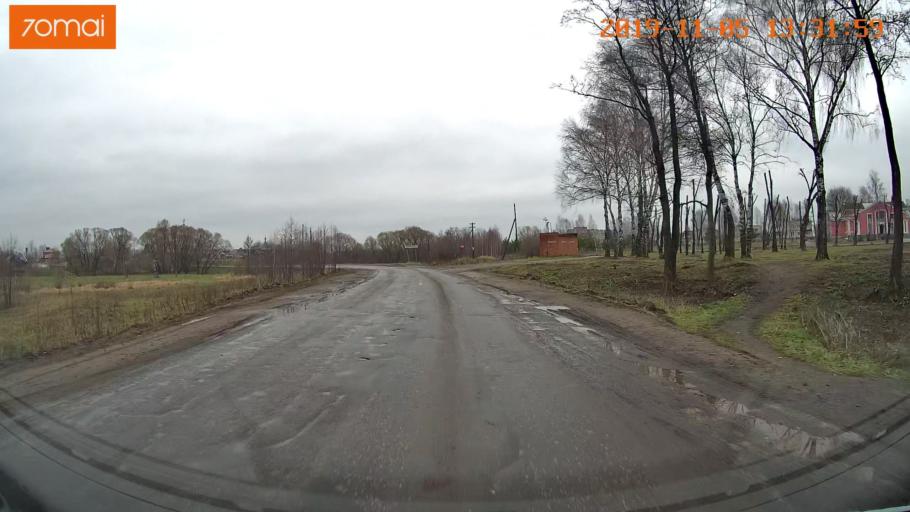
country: RU
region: Ivanovo
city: Shuya
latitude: 56.8800
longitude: 41.3974
